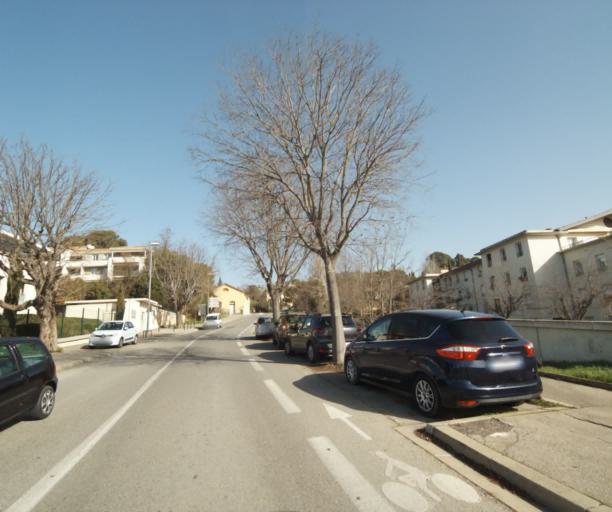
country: FR
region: Provence-Alpes-Cote d'Azur
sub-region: Departement des Bouches-du-Rhone
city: Aix-en-Provence
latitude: 43.5430
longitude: 5.4552
